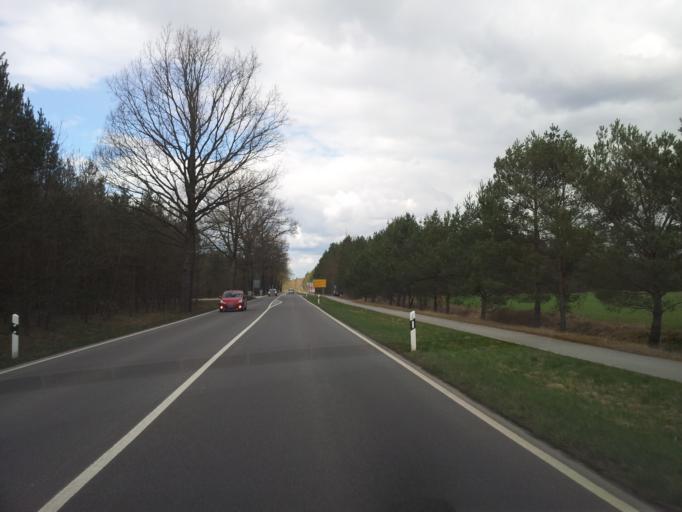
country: DE
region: Saxony
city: Wittichenau
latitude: 51.4066
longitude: 14.2913
